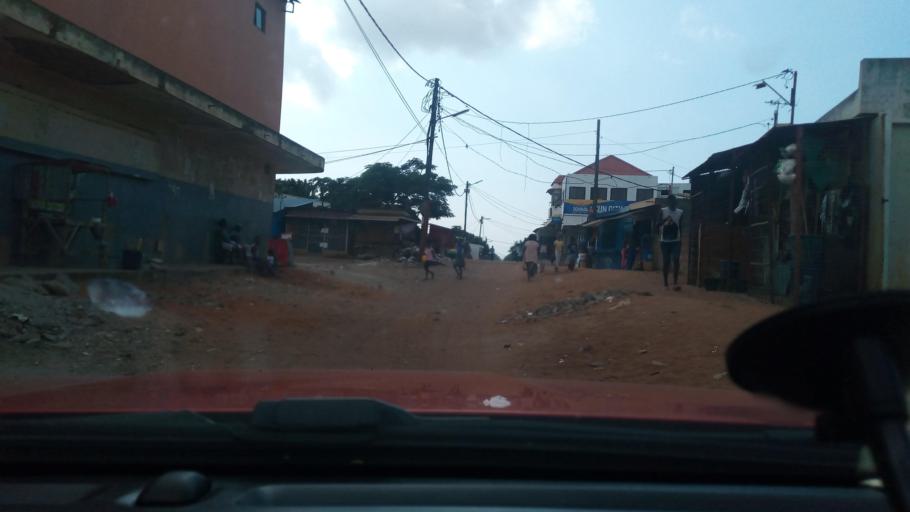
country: MZ
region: Maputo City
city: Maputo
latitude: -25.9216
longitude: 32.5940
